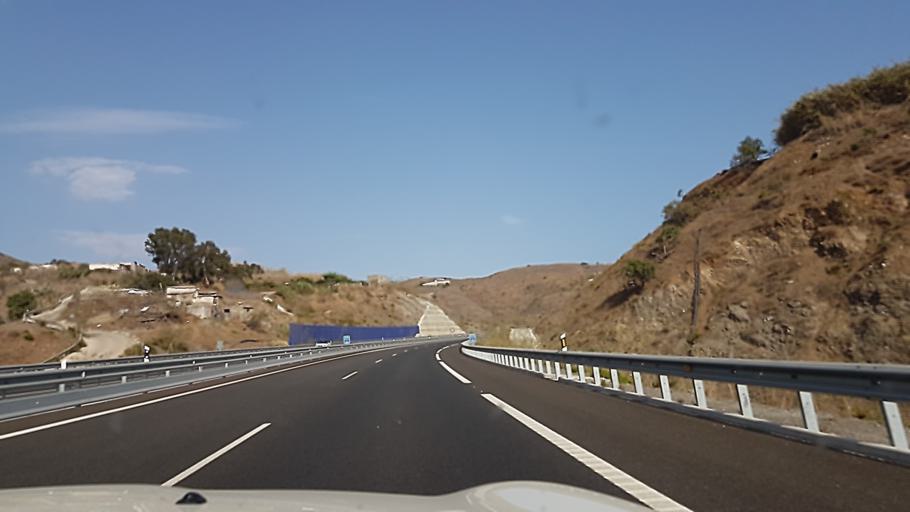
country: ES
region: Andalusia
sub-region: Provincia de Granada
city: Albunol
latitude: 36.7559
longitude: -3.2259
